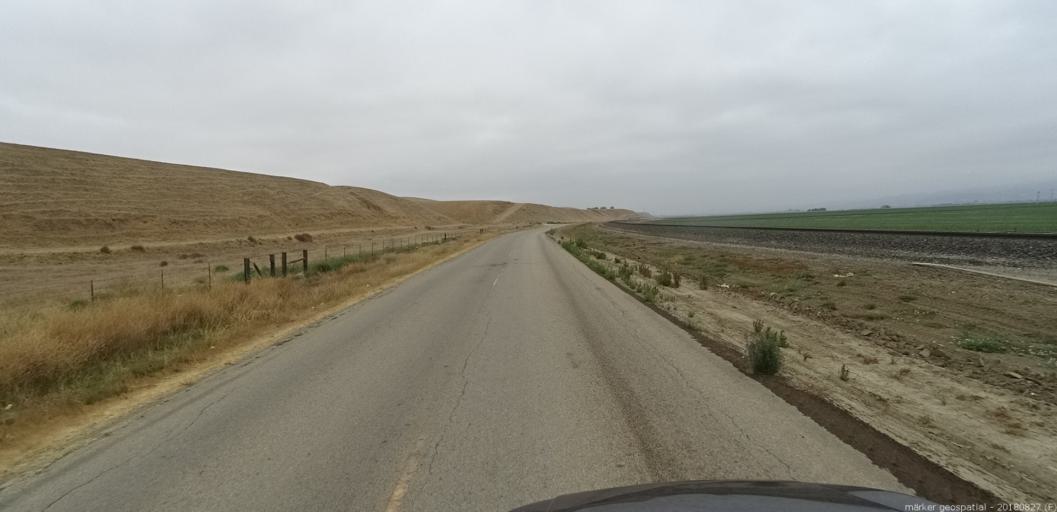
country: US
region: California
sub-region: Monterey County
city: King City
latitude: 36.2968
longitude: -121.1564
